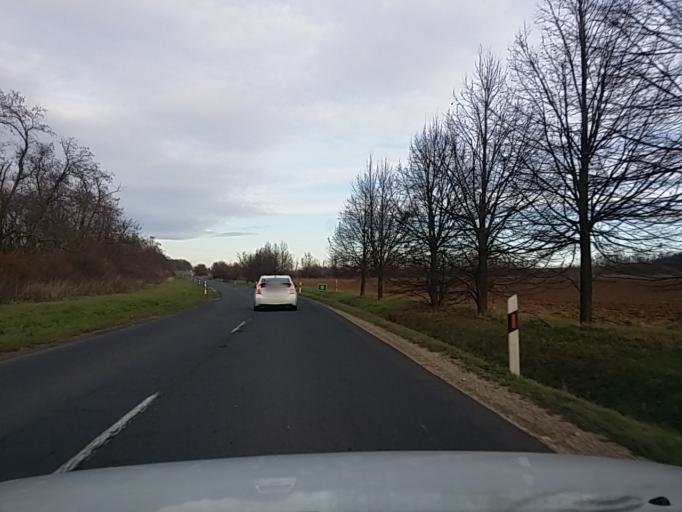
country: HU
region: Veszprem
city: Nemesvamos
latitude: 47.0269
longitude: 17.8049
